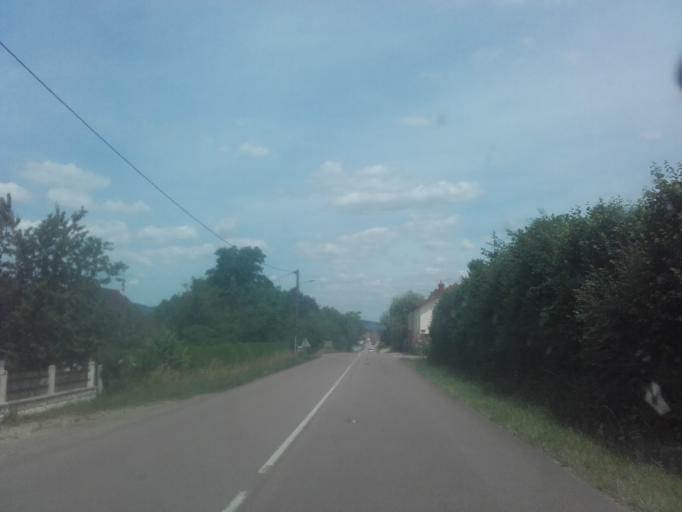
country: FR
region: Bourgogne
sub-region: Departement de Saone-et-Loire
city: Saint-Leger-sur-Dheune
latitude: 46.8707
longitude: 4.6547
